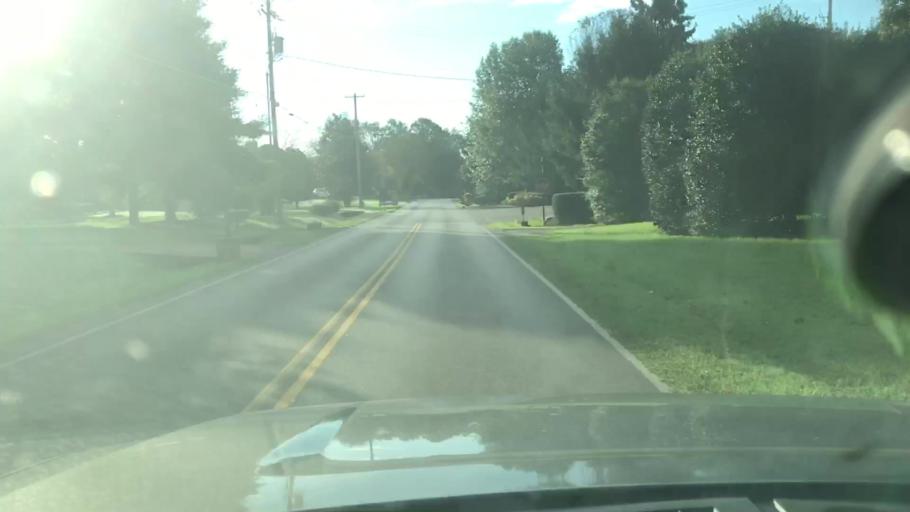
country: US
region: Tennessee
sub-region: Davidson County
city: Forest Hills
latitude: 36.0305
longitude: -86.8315
